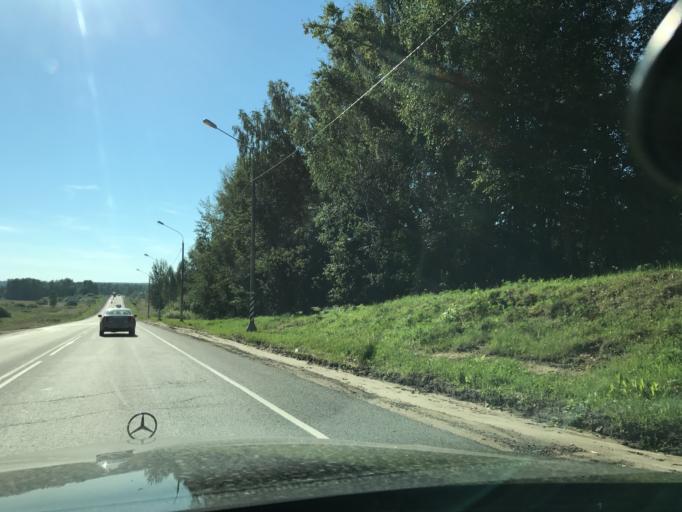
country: RU
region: Moskovskaya
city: Noginsk-9
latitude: 56.1072
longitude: 38.6269
